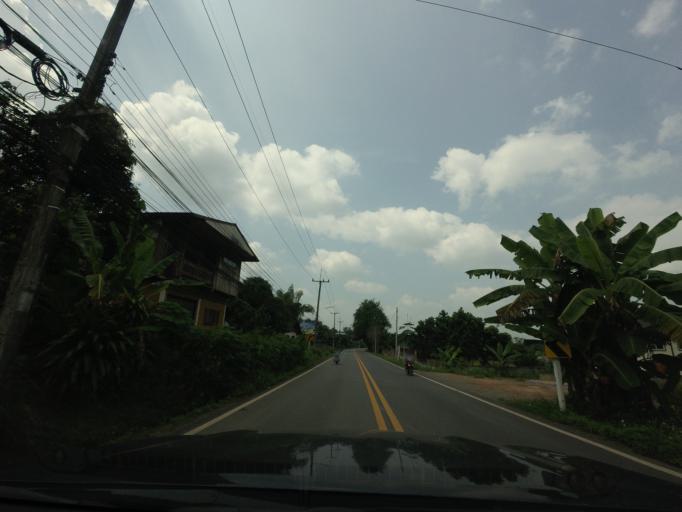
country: TH
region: Nan
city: Pua
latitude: 19.1532
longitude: 100.9336
